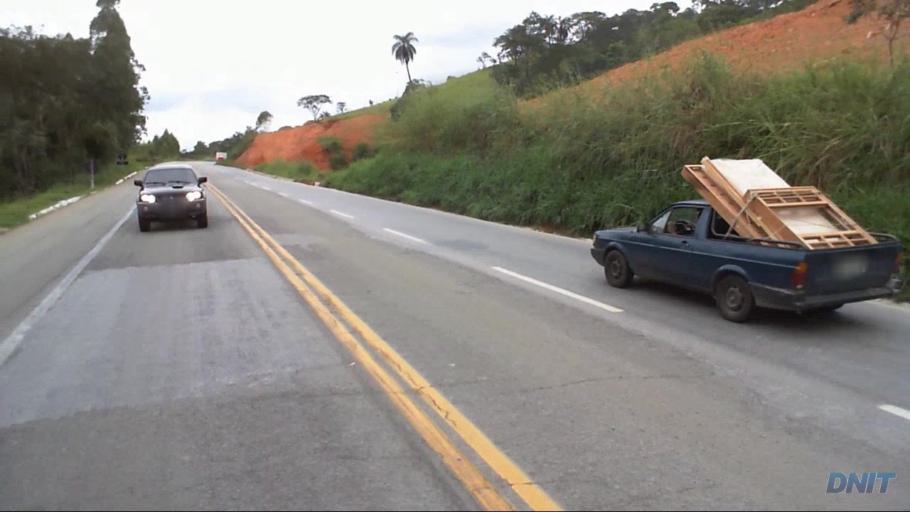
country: BR
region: Minas Gerais
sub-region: Barao De Cocais
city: Barao de Cocais
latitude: -19.7914
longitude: -43.4281
